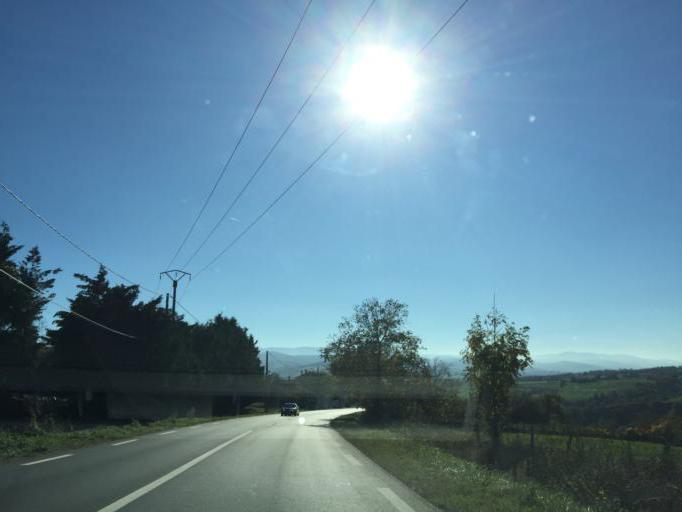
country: FR
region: Rhone-Alpes
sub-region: Departement de la Loire
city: Saint-Joseph
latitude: 45.5545
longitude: 4.6398
